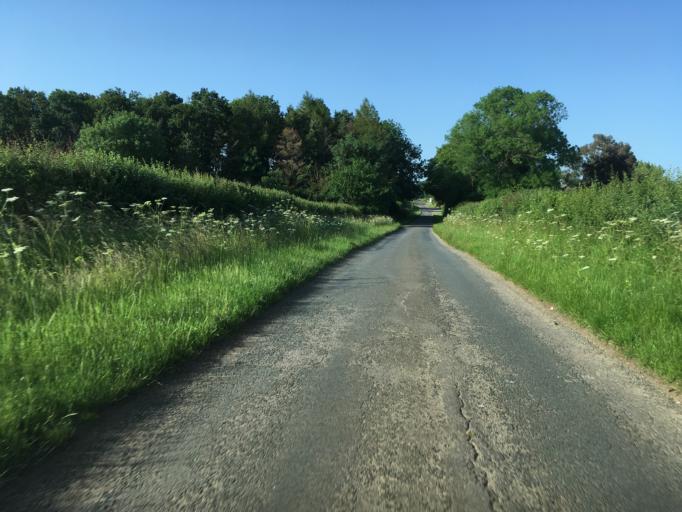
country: GB
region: England
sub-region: Gloucestershire
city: Fairford
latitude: 51.7229
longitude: -1.7607
